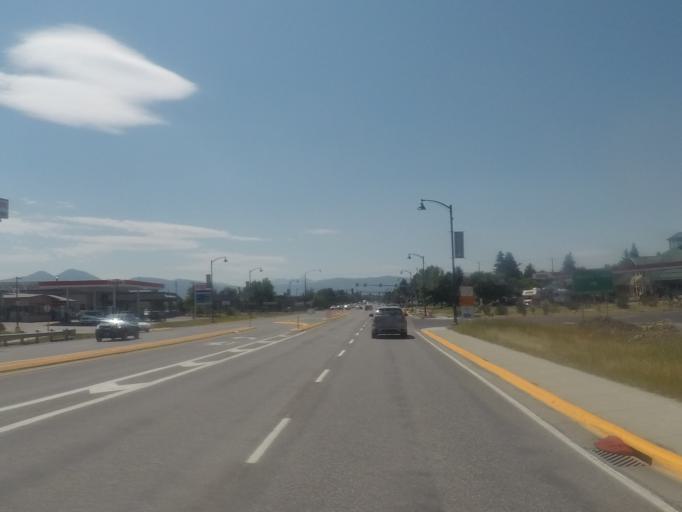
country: US
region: Montana
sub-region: Gallatin County
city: Bozeman
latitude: 45.6949
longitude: -111.0463
